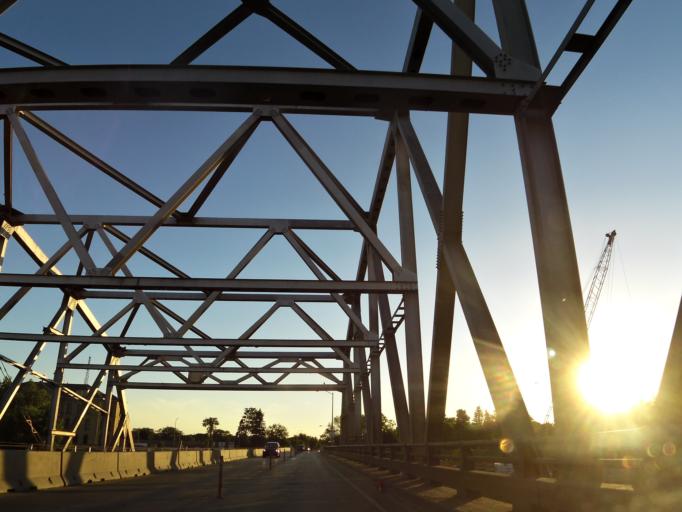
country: US
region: North Dakota
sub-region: Grand Forks County
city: Grand Forks
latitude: 47.9332
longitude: -97.0378
